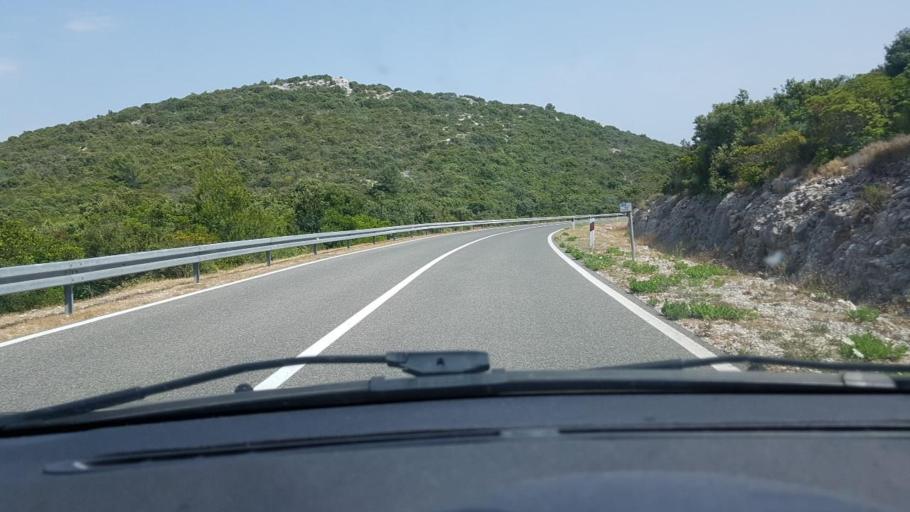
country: HR
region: Dubrovacko-Neretvanska
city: Smokvica
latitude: 42.9490
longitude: 16.9512
